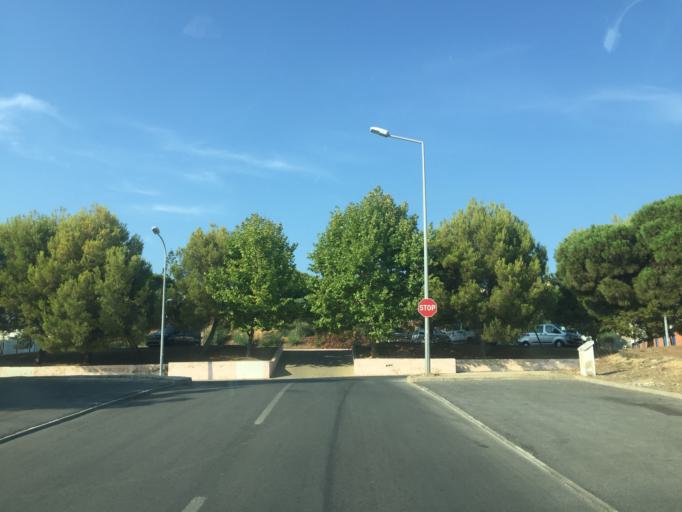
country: PT
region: Faro
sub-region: Loule
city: Quarteira
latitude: 37.0683
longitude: -8.0952
